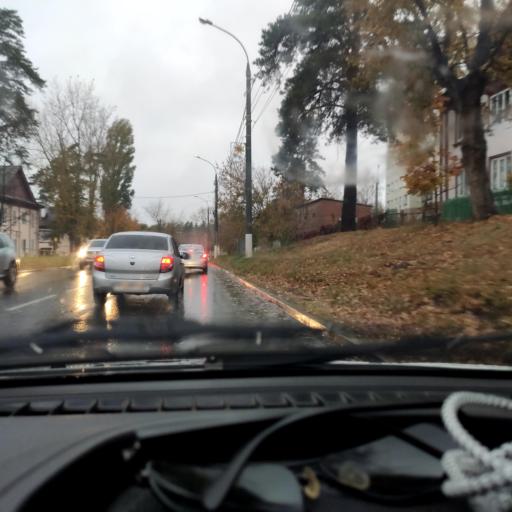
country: RU
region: Samara
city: Tol'yatti
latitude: 53.4762
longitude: 49.3702
